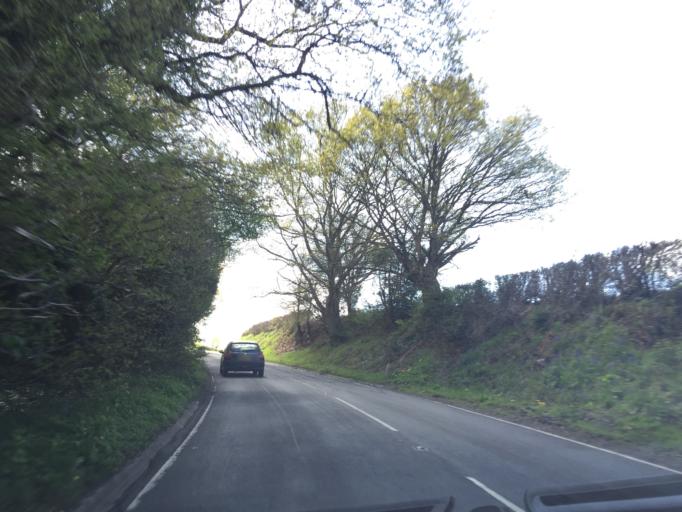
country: GB
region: England
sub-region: Kent
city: Edenbridge
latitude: 51.1397
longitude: 0.1075
